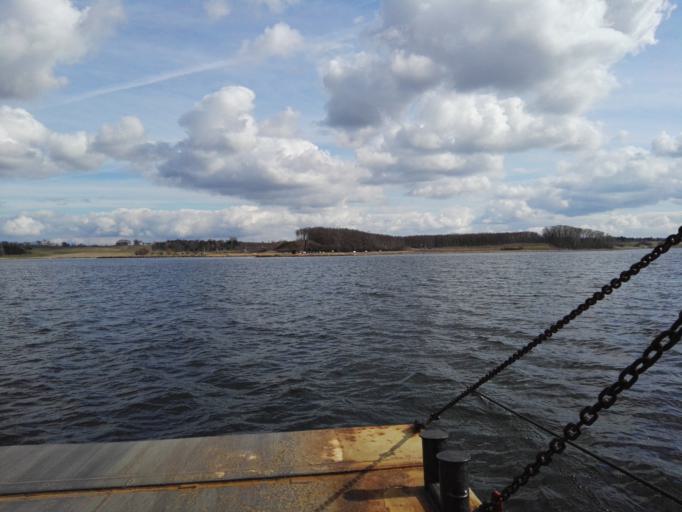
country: DK
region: Zealand
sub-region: Lejre Kommune
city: Ejby
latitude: 55.7565
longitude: 11.8408
